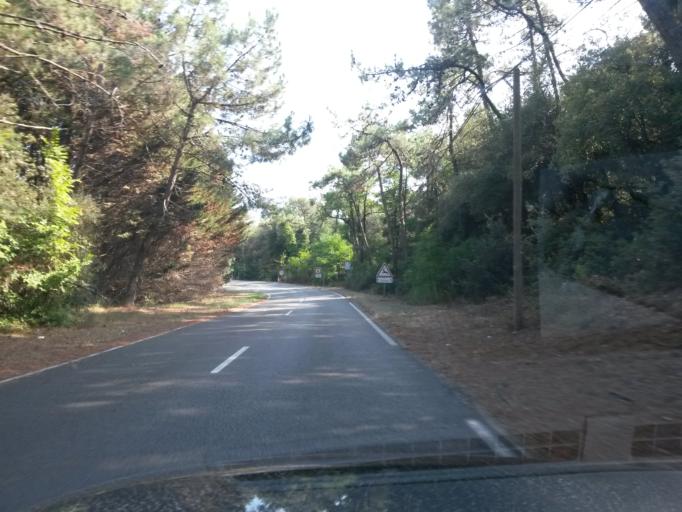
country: FR
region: Pays de la Loire
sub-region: Departement de la Vendee
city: Bretignolles-sur-Mer
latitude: 46.5860
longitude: -1.8286
